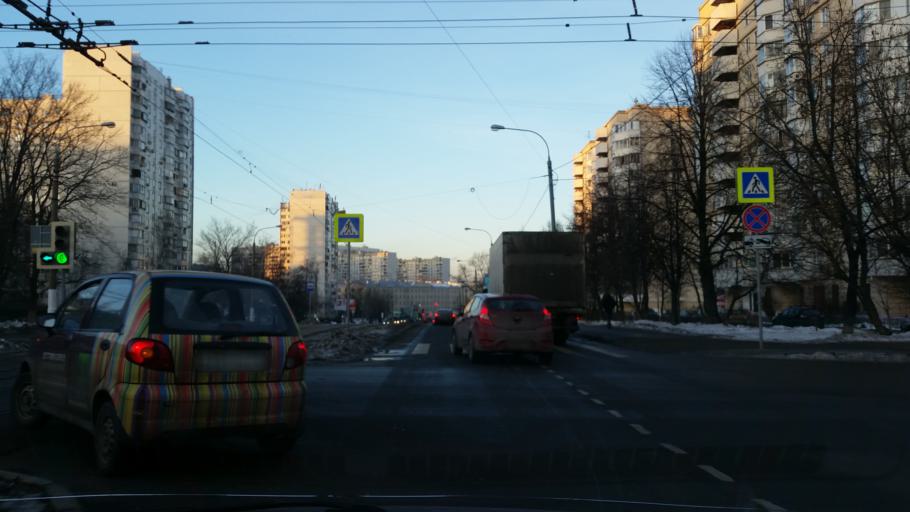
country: RU
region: Moscow
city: Kotlovka
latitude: 55.6533
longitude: 37.6056
